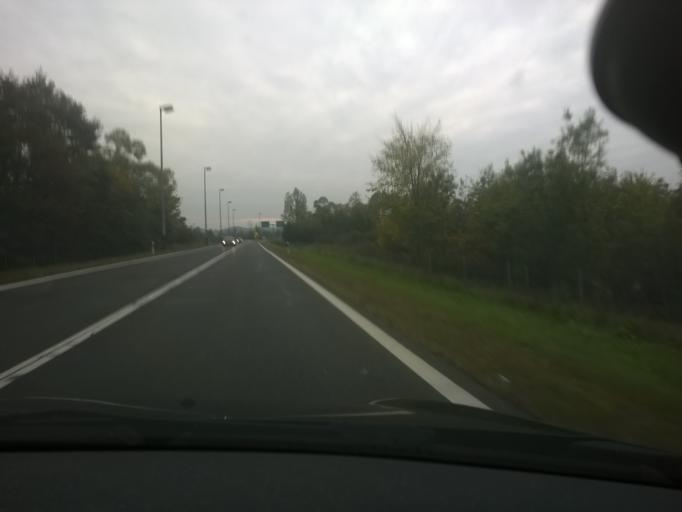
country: HR
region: Krapinsko-Zagorska
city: Oroslavje
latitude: 46.0001
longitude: 15.8703
